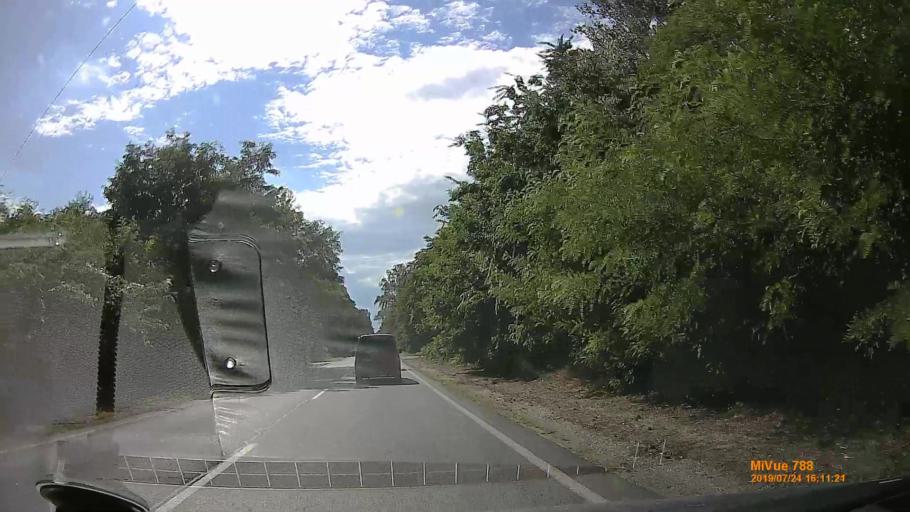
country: HU
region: Szabolcs-Szatmar-Bereg
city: Napkor
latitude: 47.9503
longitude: 21.8323
